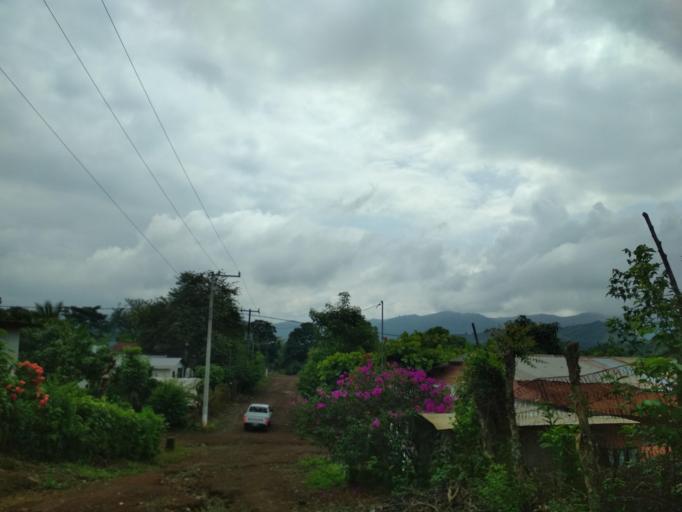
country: MX
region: Veracruz
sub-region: San Andres Tuxtla
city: Cerro las Iguanas
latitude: 18.4130
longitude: -95.1997
